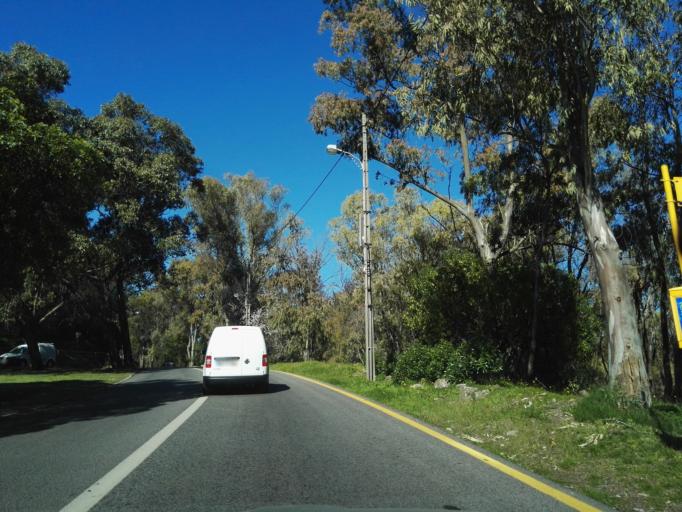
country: PT
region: Lisbon
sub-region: Odivelas
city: Pontinha
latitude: 38.7234
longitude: -9.1872
